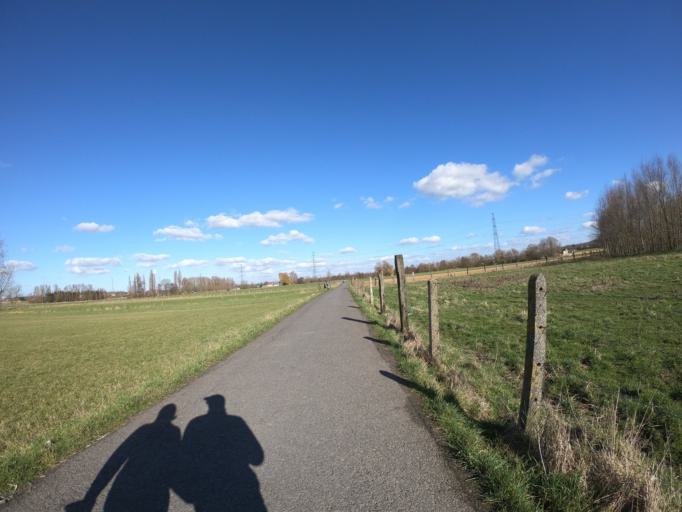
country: BE
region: Flanders
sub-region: Provincie West-Vlaanderen
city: Avelgem
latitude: 50.7710
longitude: 3.4620
